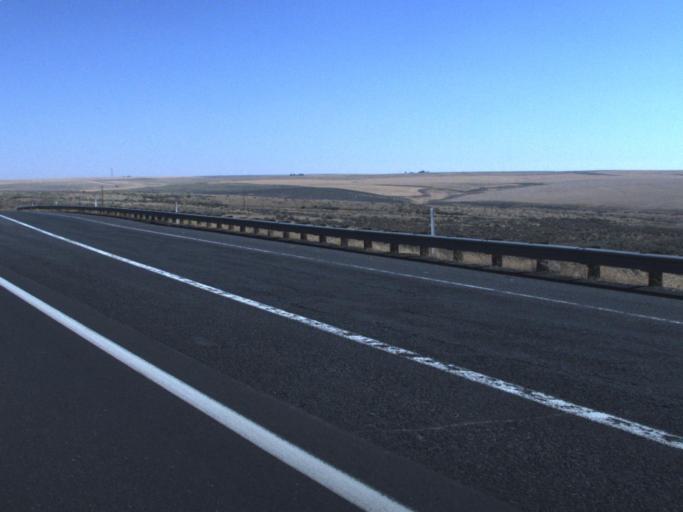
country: US
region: Washington
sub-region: Adams County
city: Ritzville
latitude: 47.0970
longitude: -118.6743
